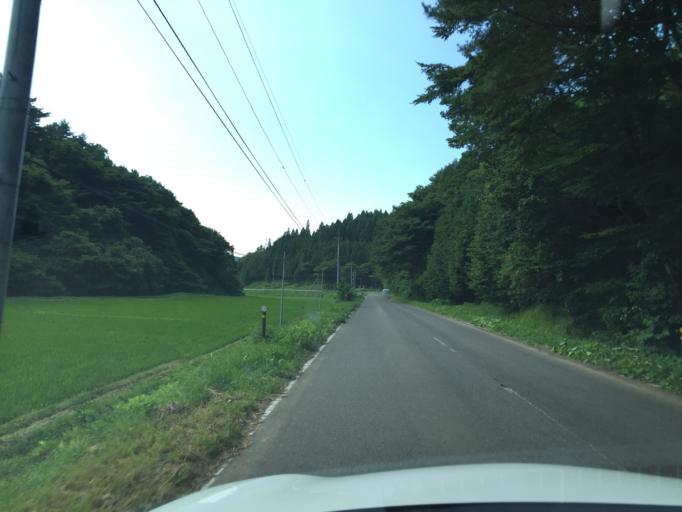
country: JP
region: Fukushima
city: Ishikawa
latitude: 37.1649
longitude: 140.6262
